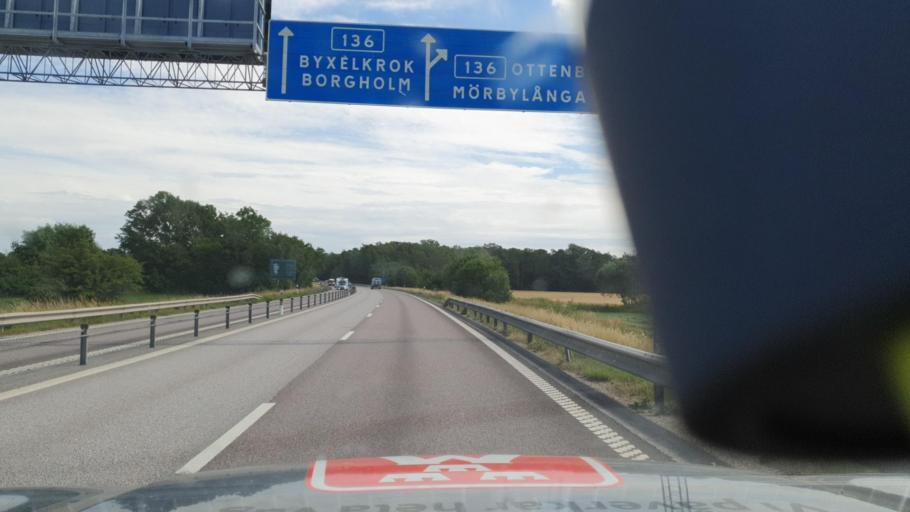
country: SE
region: Kalmar
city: Faerjestaden
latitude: 56.6681
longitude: 16.5039
